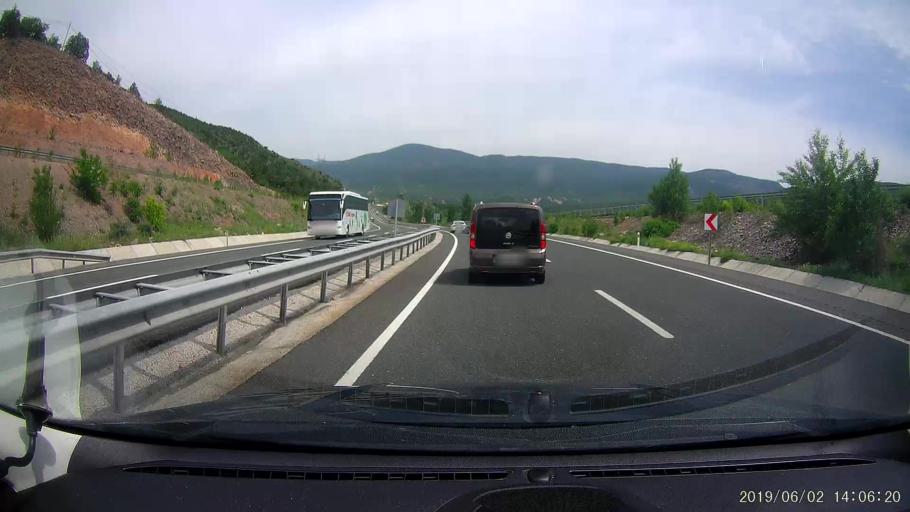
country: TR
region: Cankiri
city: Ilgaz
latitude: 40.8901
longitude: 33.6787
